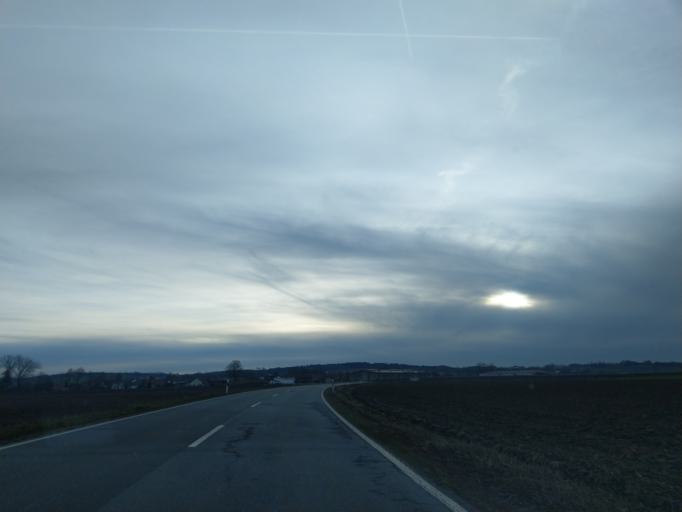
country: DE
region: Bavaria
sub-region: Lower Bavaria
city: Wallerfing
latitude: 48.7015
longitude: 12.8828
